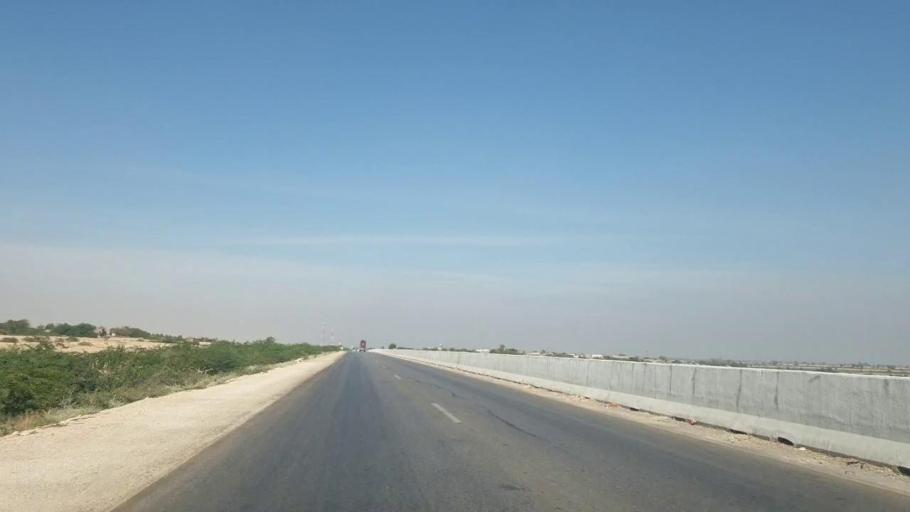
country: PK
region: Sindh
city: Hala
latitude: 25.6914
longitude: 68.2954
